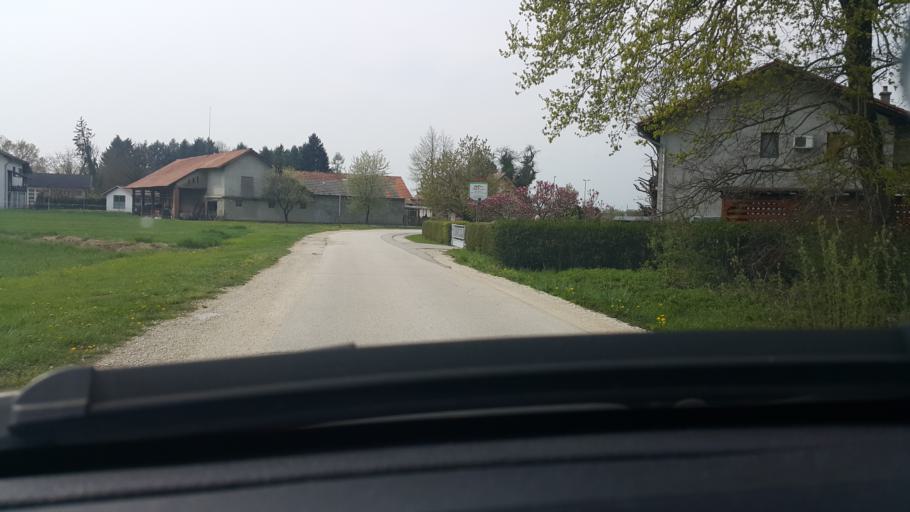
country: SI
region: Brezice
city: Brezice
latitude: 45.9117
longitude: 15.6224
